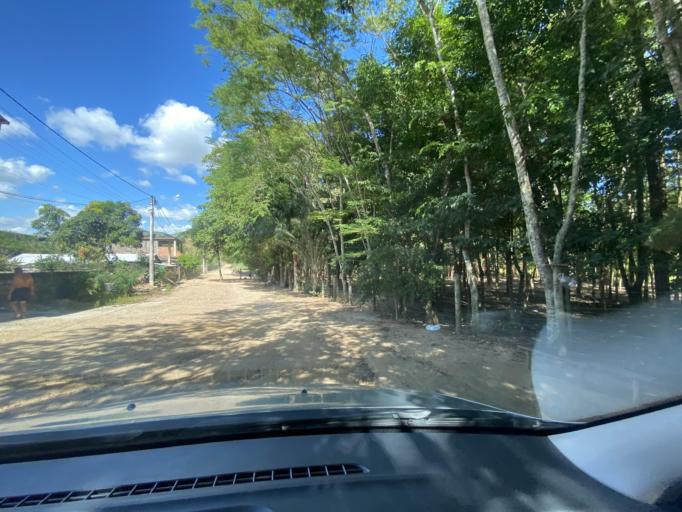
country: BR
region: Espirito Santo
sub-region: Jeronimo Monteiro
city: Jeronimo Monteiro
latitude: -20.7964
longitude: -41.4060
